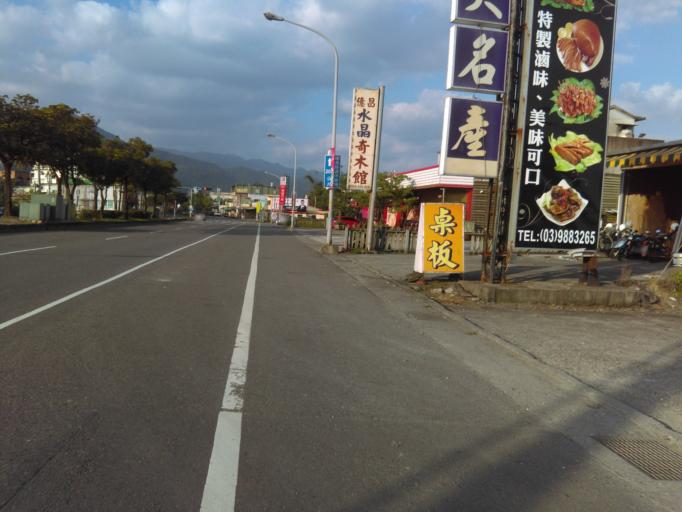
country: TW
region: Taiwan
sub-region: Yilan
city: Yilan
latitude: 24.8078
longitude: 121.7668
